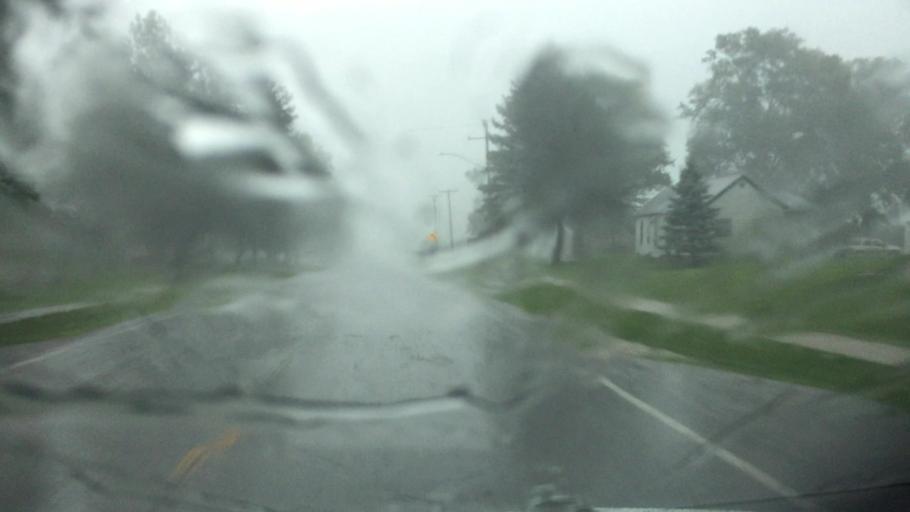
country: US
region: Illinois
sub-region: Hancock County
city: Carthage
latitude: 40.2349
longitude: -91.0645
